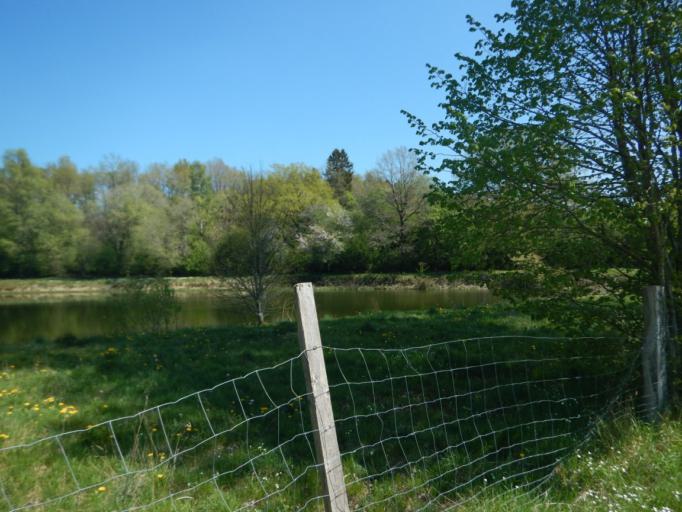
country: LU
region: Diekirch
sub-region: Canton de Clervaux
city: Troisvierges
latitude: 50.1439
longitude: 6.0156
